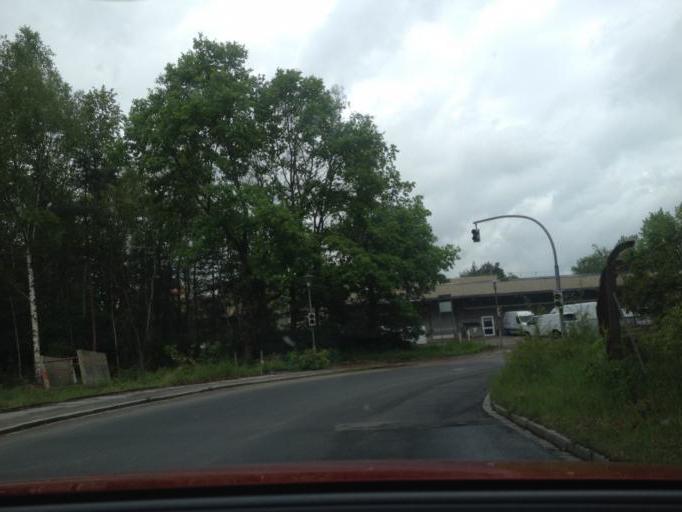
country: DE
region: Bavaria
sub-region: Regierungsbezirk Mittelfranken
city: Rothenbach an der Pegnitz
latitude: 49.4783
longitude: 11.2354
